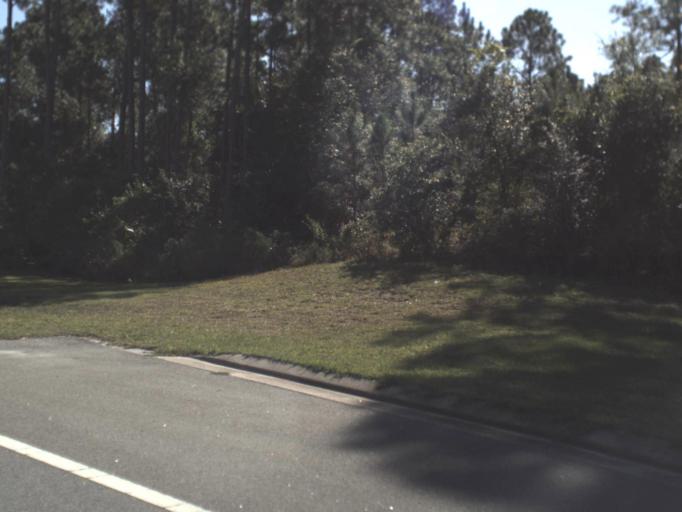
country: US
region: Florida
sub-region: Flagler County
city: Palm Coast
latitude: 29.5508
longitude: -81.2412
